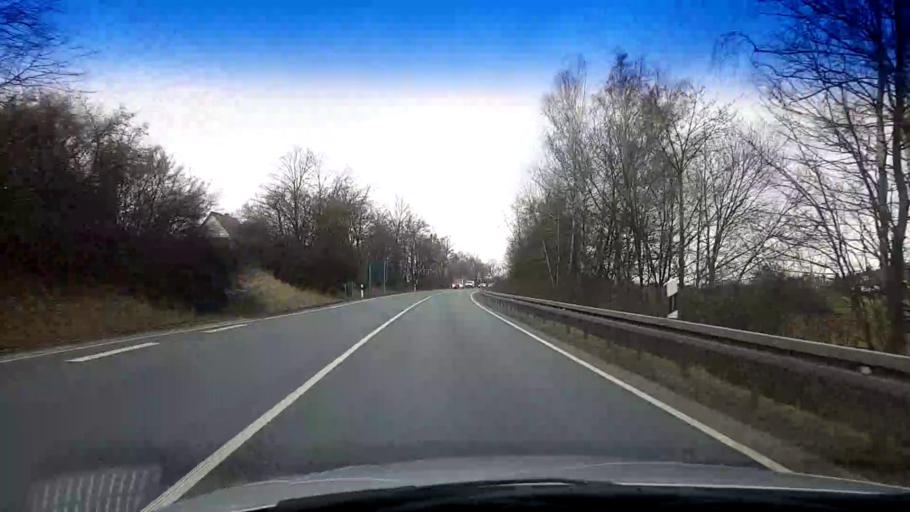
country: DE
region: Bavaria
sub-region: Upper Franconia
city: Kulmbach
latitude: 50.0803
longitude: 11.4651
